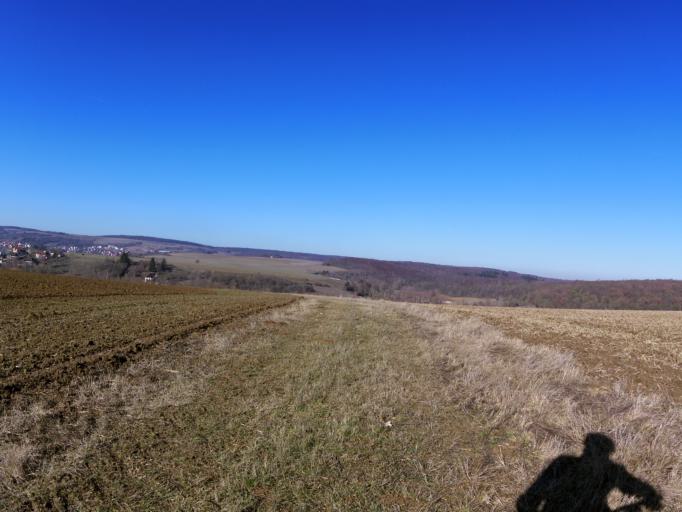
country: DE
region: Bavaria
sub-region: Regierungsbezirk Unterfranken
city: Rimpar
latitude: 49.8455
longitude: 9.9829
